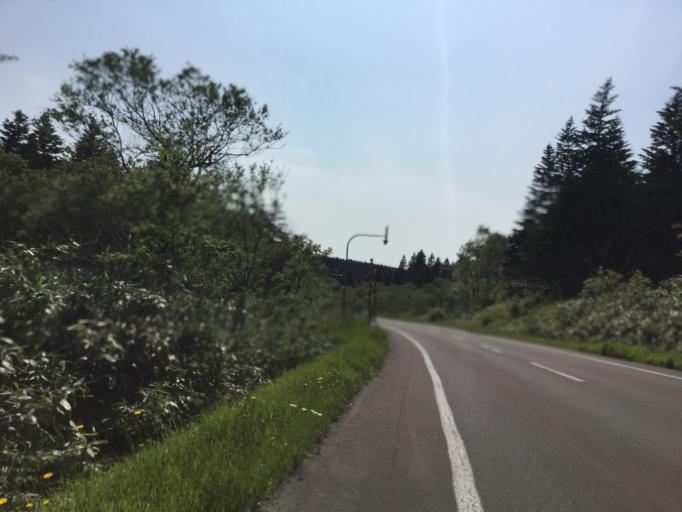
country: JP
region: Hokkaido
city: Makubetsu
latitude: 45.4118
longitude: 141.9722
